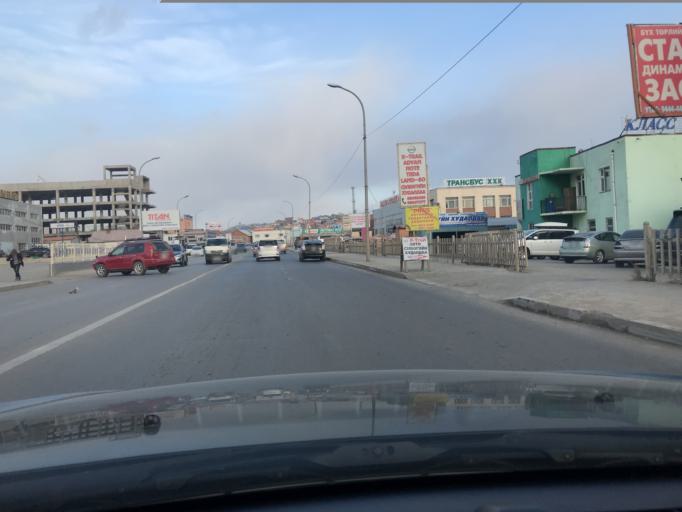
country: MN
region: Ulaanbaatar
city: Ulaanbaatar
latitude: 47.9240
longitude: 106.9927
